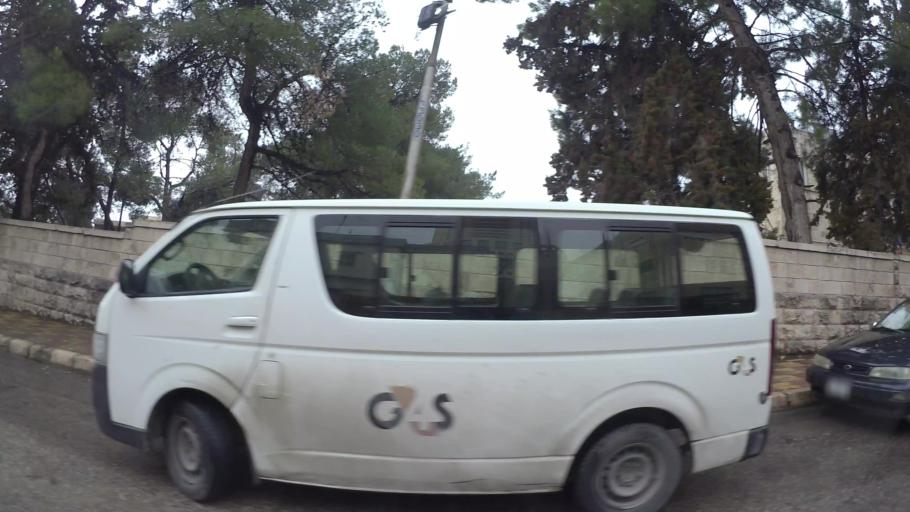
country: JO
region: Amman
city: Amman
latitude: 31.9521
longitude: 35.9084
